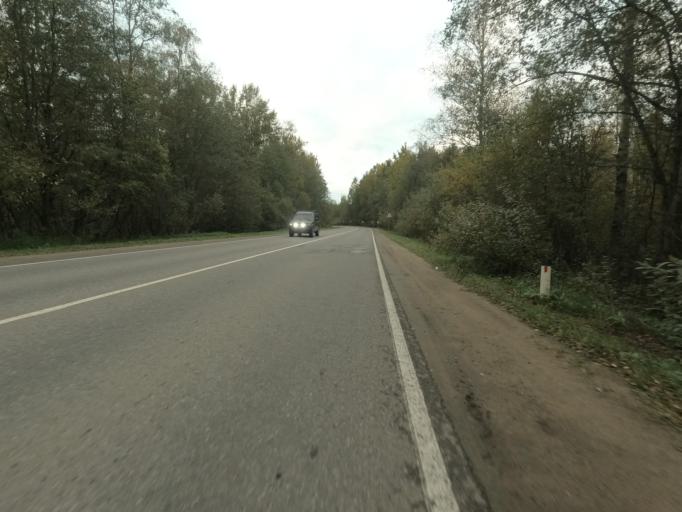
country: RU
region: Leningrad
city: Pavlovo
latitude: 59.8039
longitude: 30.9359
